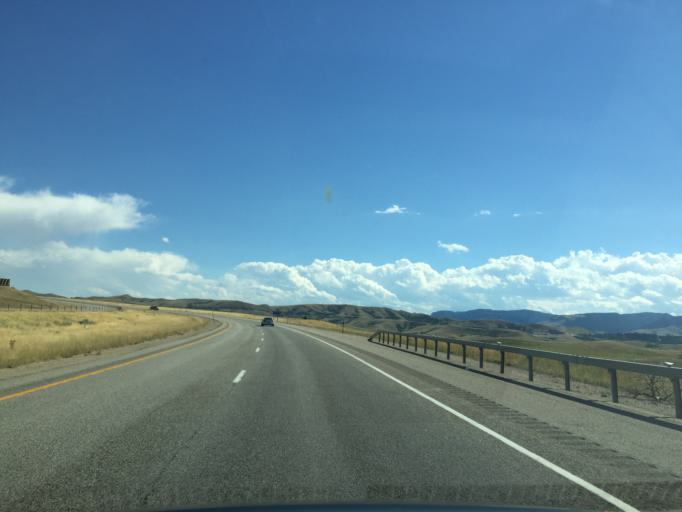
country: US
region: Wyoming
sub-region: Sheridan County
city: Sheridan
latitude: 44.6071
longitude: -106.8481
